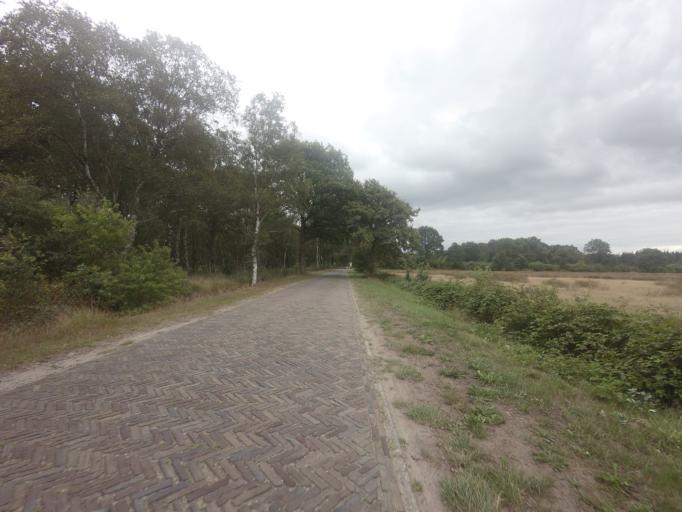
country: NL
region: Drenthe
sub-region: Gemeente Westerveld
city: Havelte
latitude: 52.8831
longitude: 6.2636
